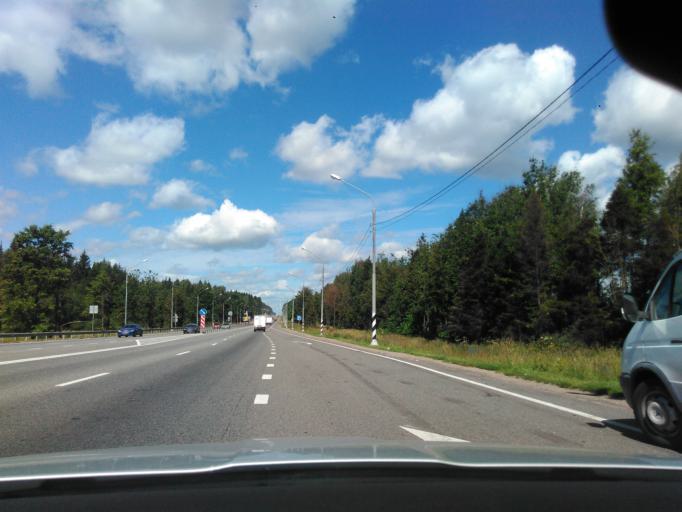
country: RU
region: Moskovskaya
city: Solnechnogorsk
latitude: 56.2529
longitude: 36.8726
